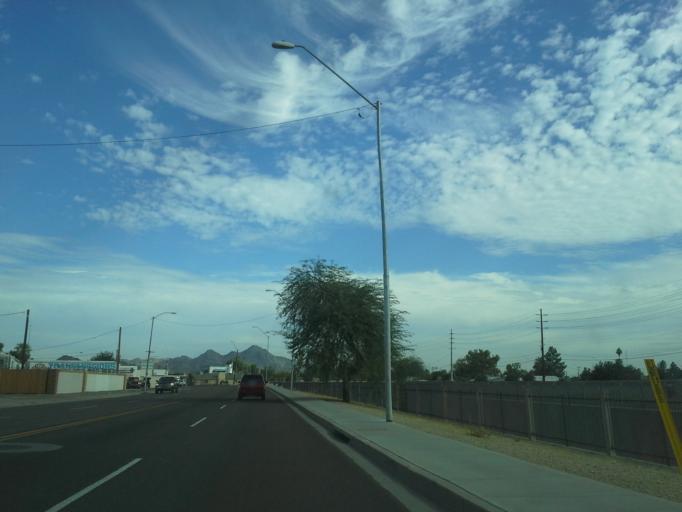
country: US
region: Arizona
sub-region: Maricopa County
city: Glendale
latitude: 33.5717
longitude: -112.0974
